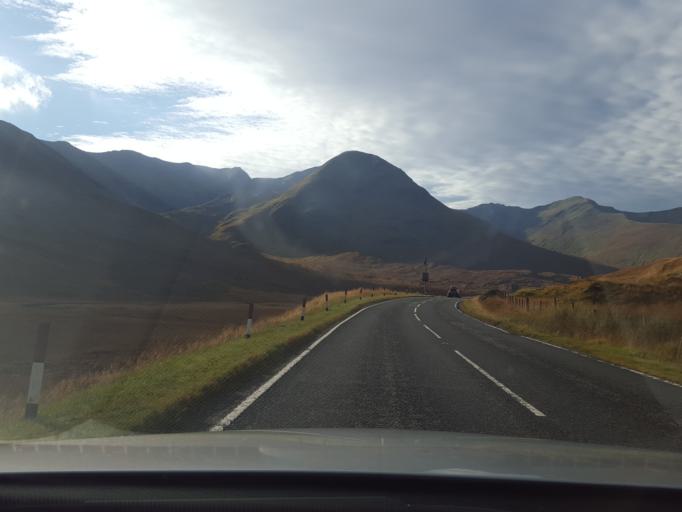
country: GB
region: Scotland
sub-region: Highland
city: Fort William
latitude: 57.1555
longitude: -5.1843
